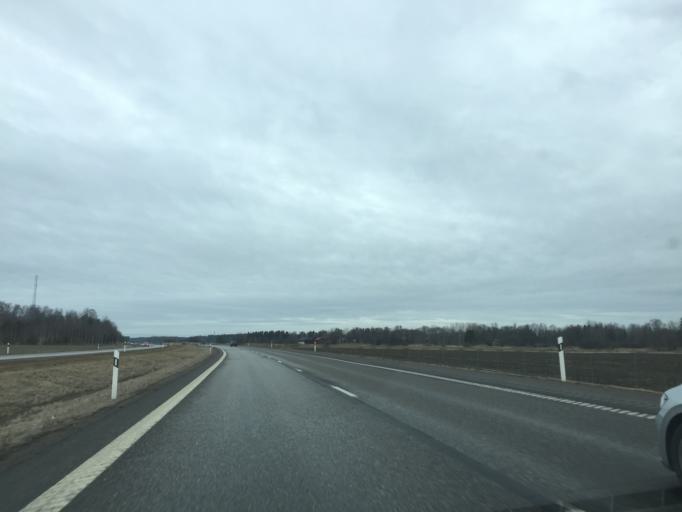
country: SE
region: Vaestmanland
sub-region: Arboga Kommun
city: Arboga
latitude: 59.4414
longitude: 15.9005
